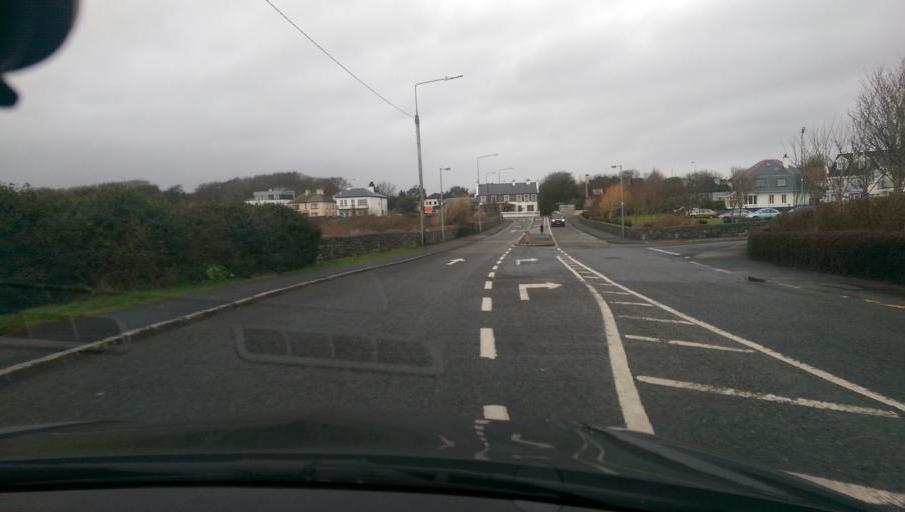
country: IE
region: Connaught
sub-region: County Galway
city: Bearna
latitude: 53.2597
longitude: -9.1077
